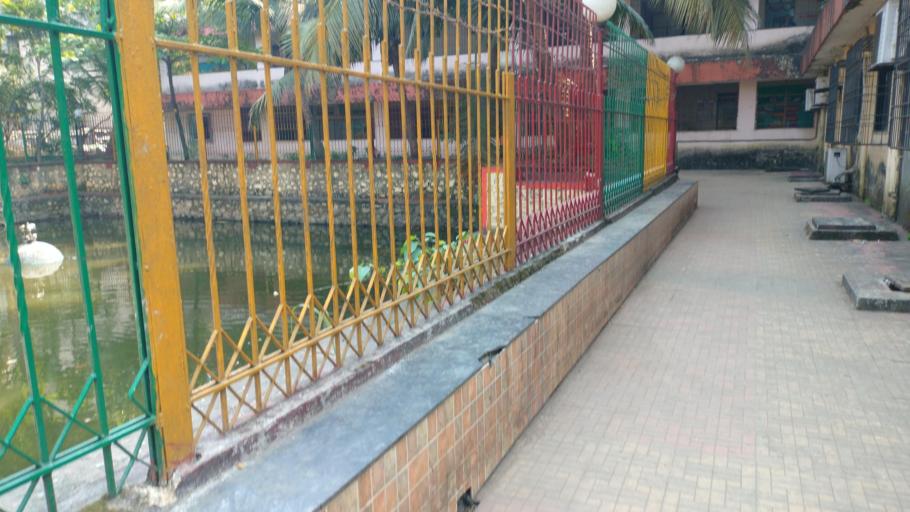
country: IN
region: Maharashtra
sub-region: Thane
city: Bhayandar
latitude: 19.3091
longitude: 72.8576
